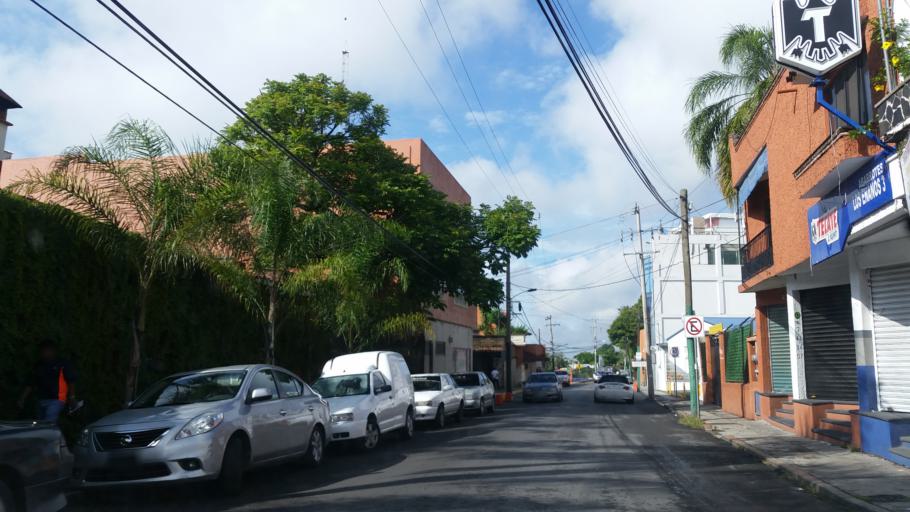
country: MX
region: Morelos
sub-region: Cuernavaca
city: Cuernavaca
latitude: 18.9198
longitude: -99.2179
